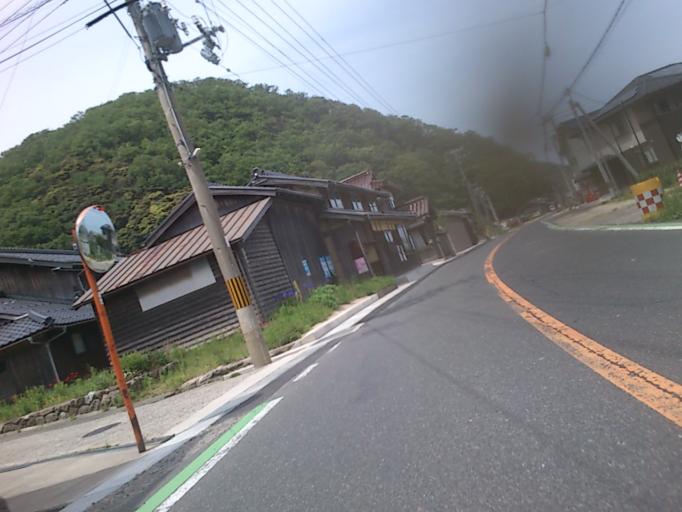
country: JP
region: Kyoto
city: Miyazu
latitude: 35.7250
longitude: 135.0981
